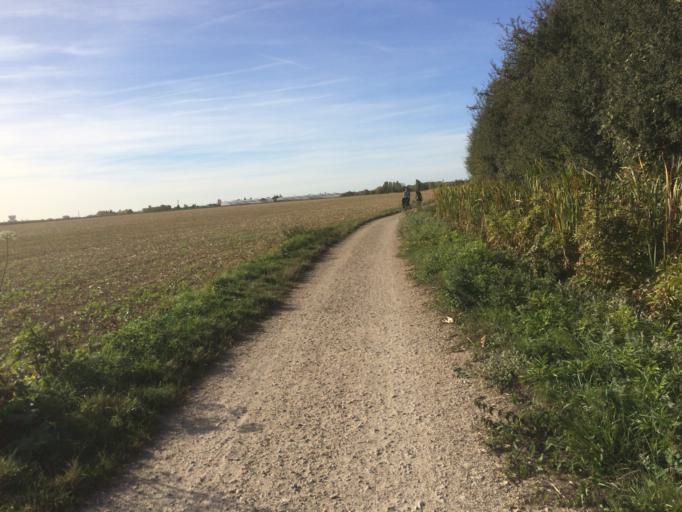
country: FR
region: Ile-de-France
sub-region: Departement de l'Essonne
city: Vauhallan
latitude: 48.7271
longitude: 2.1945
